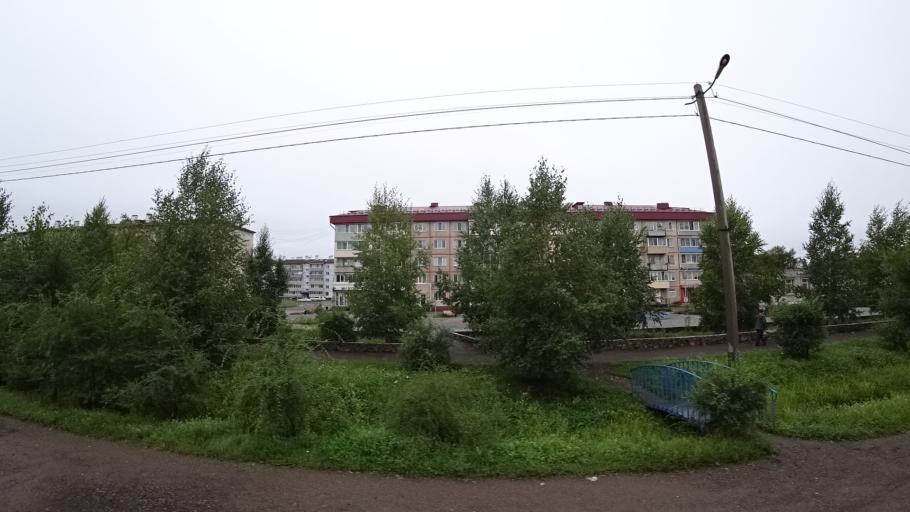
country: RU
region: Primorskiy
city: Monastyrishche
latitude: 44.2043
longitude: 132.4464
